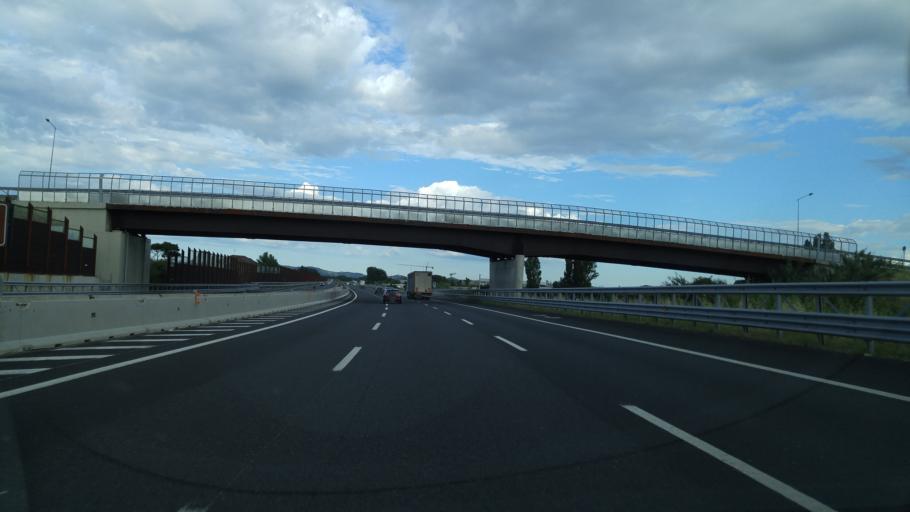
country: IT
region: Emilia-Romagna
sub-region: Provincia di Rimini
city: Santa Monica-Cella
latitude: 43.9695
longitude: 12.6703
